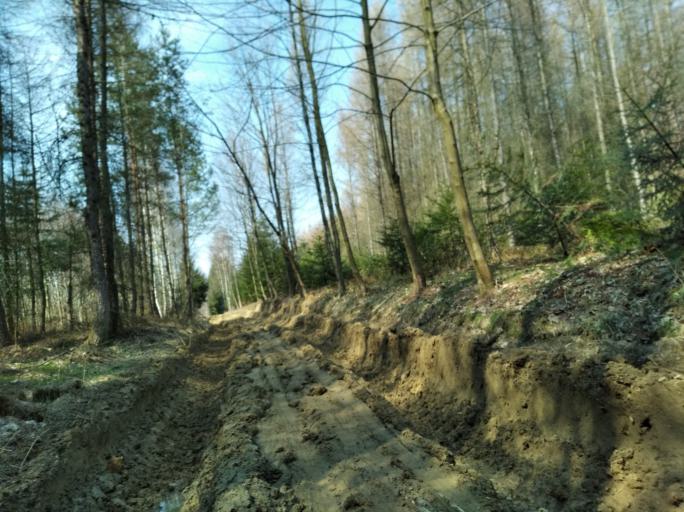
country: PL
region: Subcarpathian Voivodeship
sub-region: Powiat strzyzowski
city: Wysoka Strzyzowska
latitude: 49.8081
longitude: 21.7944
